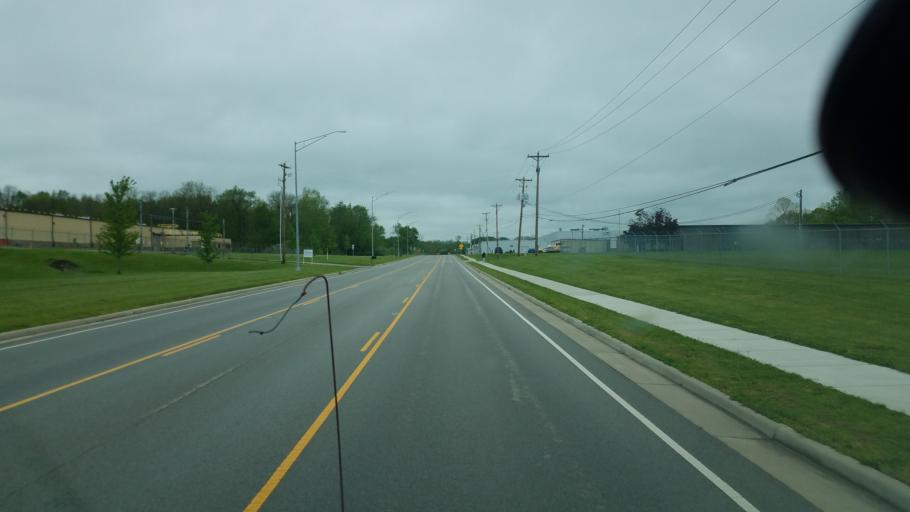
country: US
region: Ohio
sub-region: Highland County
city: Hillsboro
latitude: 39.2346
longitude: -83.6140
